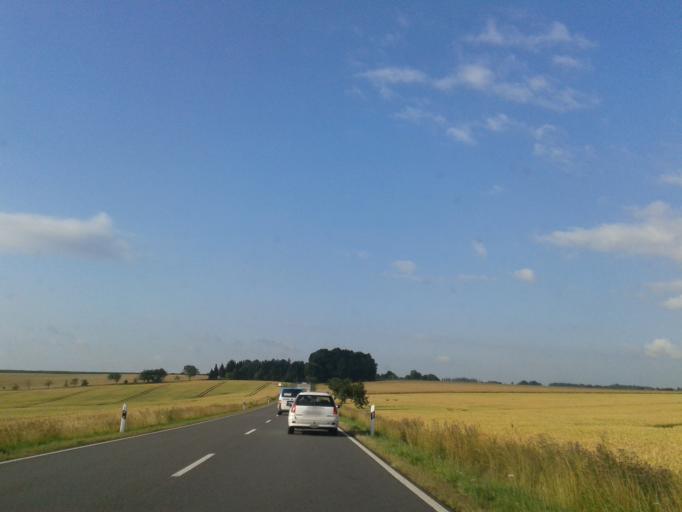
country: DE
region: Saxony
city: Niederschona
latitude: 50.9871
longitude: 13.4482
